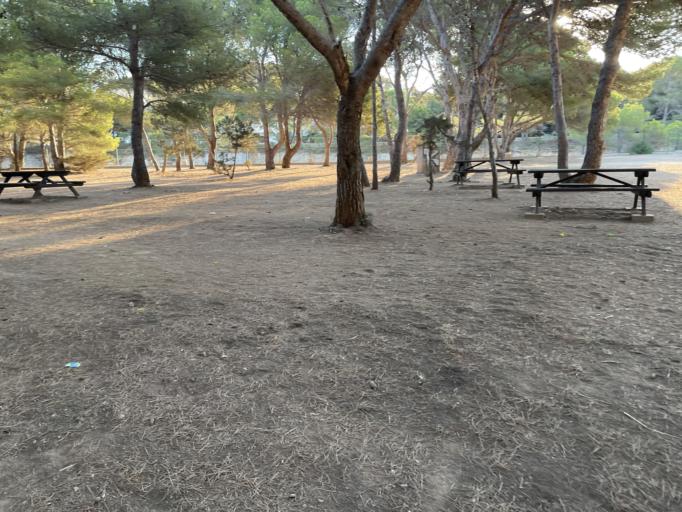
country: ES
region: Balearic Islands
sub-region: Illes Balears
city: Capdepera
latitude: 39.7170
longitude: 3.4643
